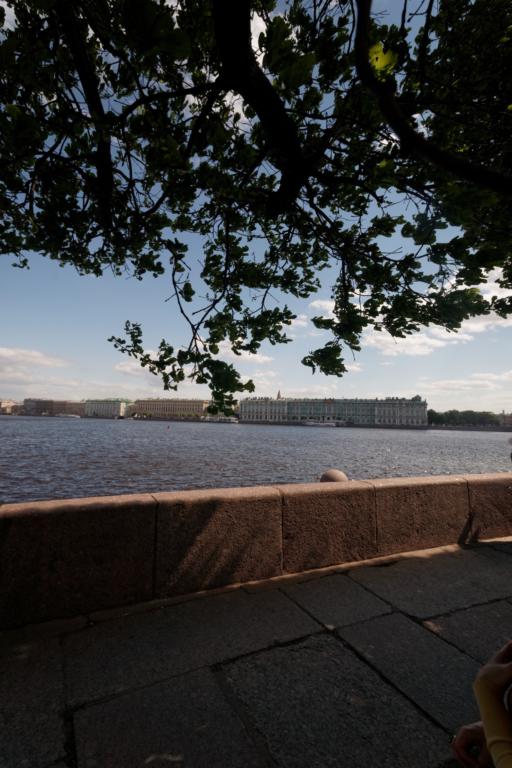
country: RU
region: St.-Petersburg
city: Saint Petersburg
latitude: 59.9444
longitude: 30.3072
